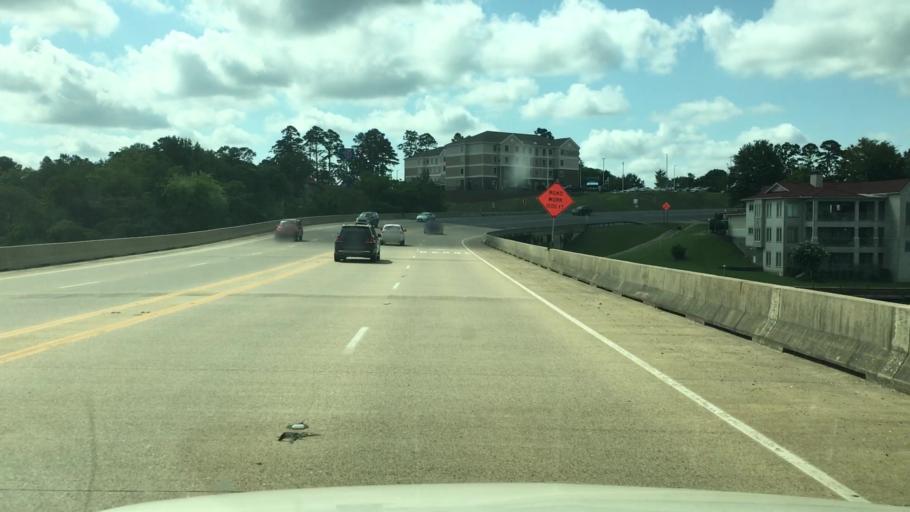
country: US
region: Arkansas
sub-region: Garland County
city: Lake Hamilton
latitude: 34.4304
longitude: -93.0855
